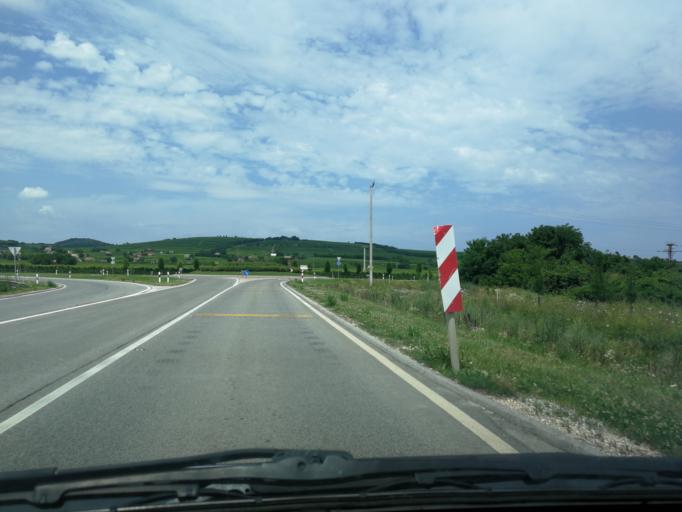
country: HU
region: Baranya
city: Villany
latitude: 45.8607
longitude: 18.4437
